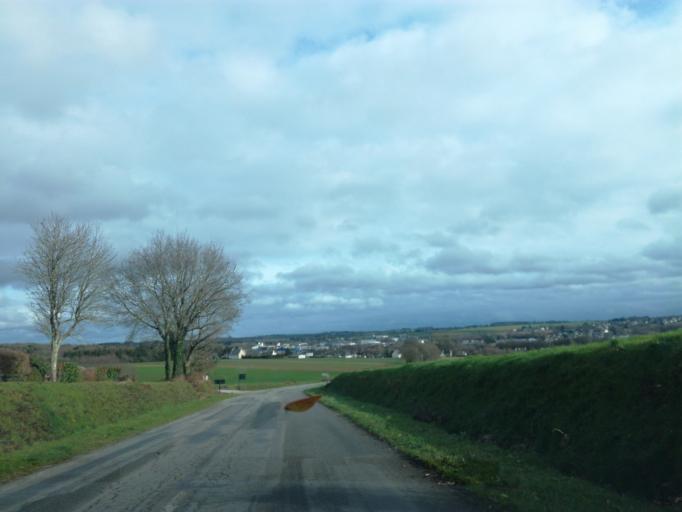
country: FR
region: Brittany
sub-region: Departement du Morbihan
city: Le Sourn
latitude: 48.0407
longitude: -2.9804
